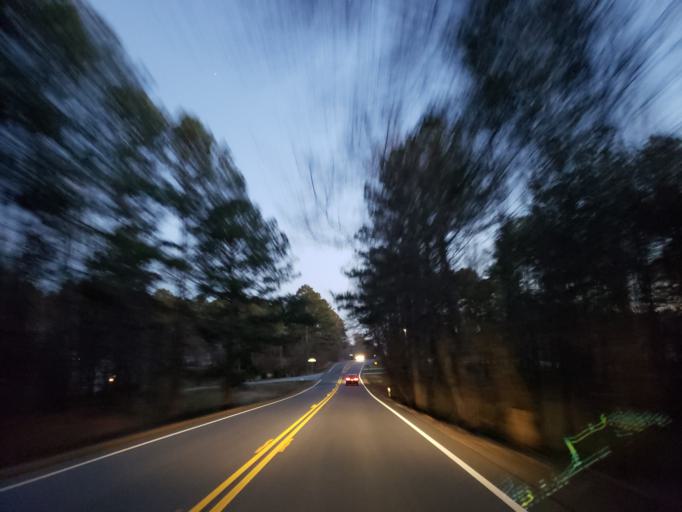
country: US
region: Georgia
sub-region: Bartow County
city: Emerson
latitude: 34.0739
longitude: -84.8307
